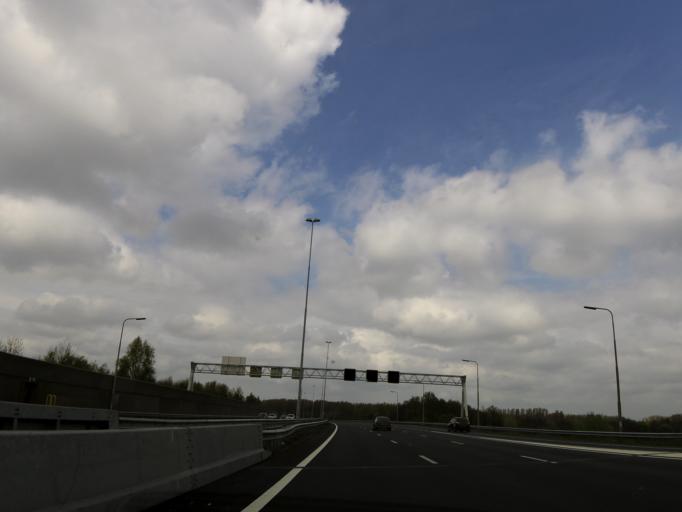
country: NL
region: North Brabant
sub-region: Gemeente Boxtel
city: Boxtel
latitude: 51.5802
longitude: 5.3560
